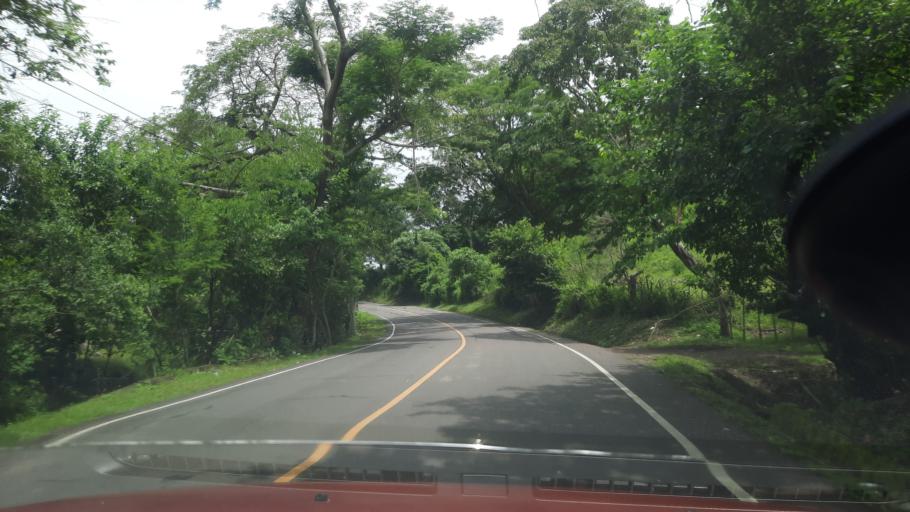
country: SV
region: La Union
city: Santa Rosa de Lima
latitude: 13.6522
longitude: -87.8402
